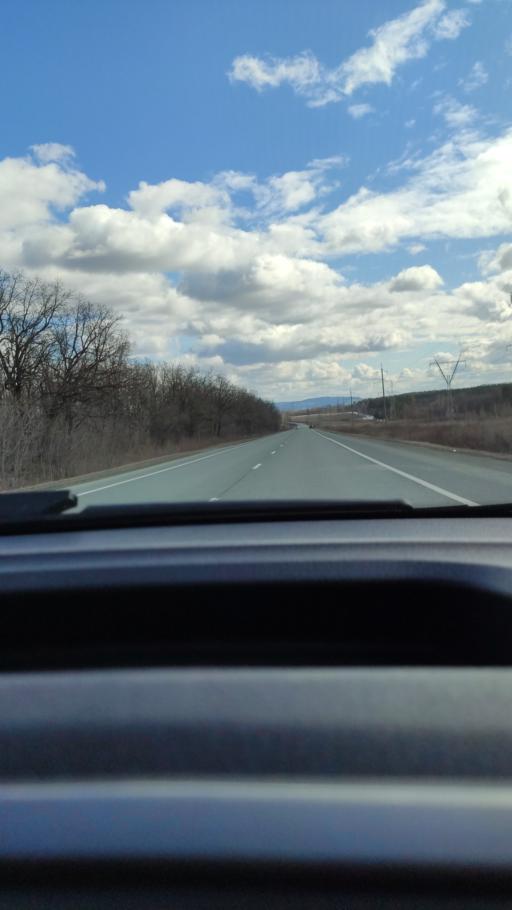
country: RU
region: Samara
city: Bogatyr'
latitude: 53.4986
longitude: 49.9566
